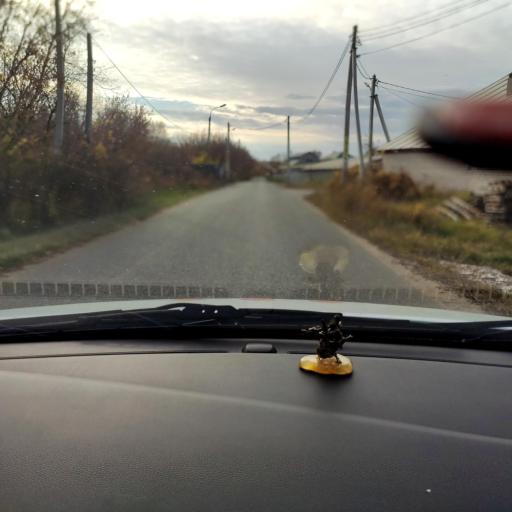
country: RU
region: Tatarstan
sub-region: Gorod Kazan'
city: Kazan
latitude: 55.7375
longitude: 49.0995
